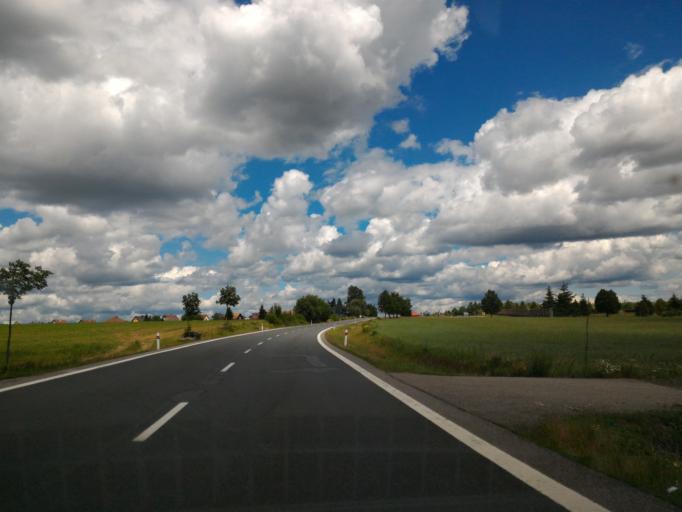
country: CZ
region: Vysocina
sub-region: Okres Zd'ar nad Sazavou
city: Nove Veseli
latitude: 49.5119
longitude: 15.9010
